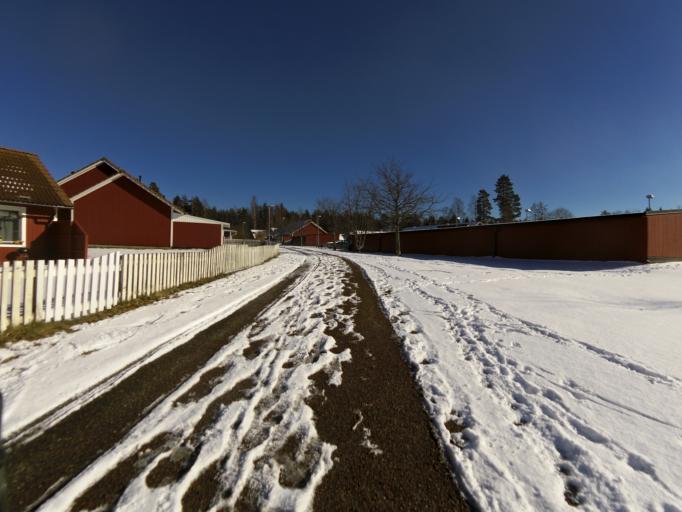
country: SE
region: Gaevleborg
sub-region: Gavle Kommun
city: Gavle
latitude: 60.6616
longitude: 17.2301
